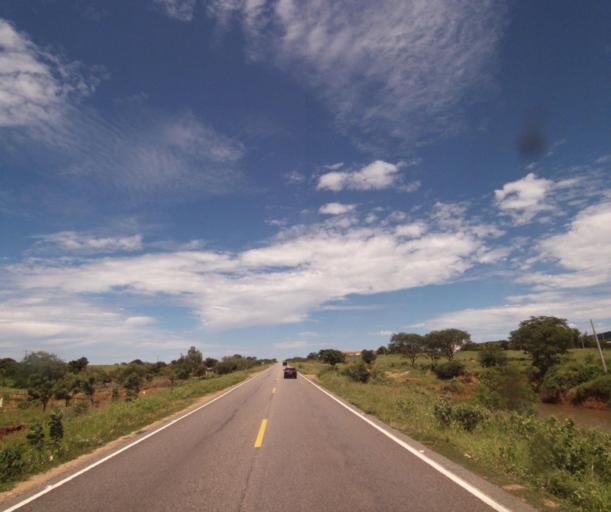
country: BR
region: Bahia
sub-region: Palmas De Monte Alto
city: Palmas de Monte Alto
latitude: -14.2487
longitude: -43.1520
